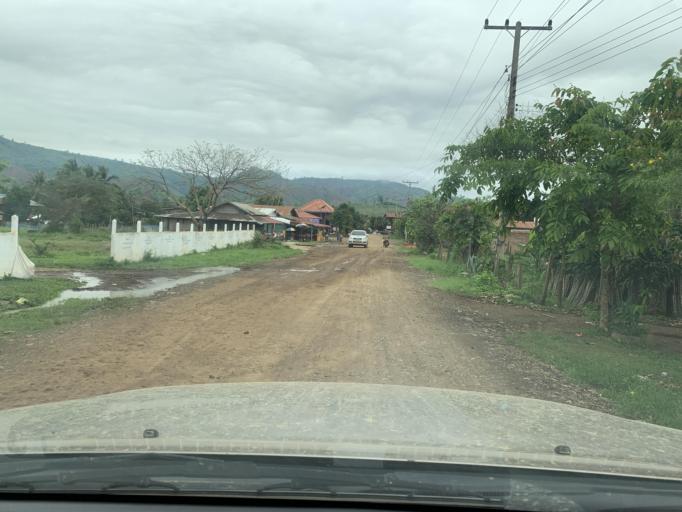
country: TH
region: Nan
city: Mae Charim
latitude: 18.4196
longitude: 101.4510
